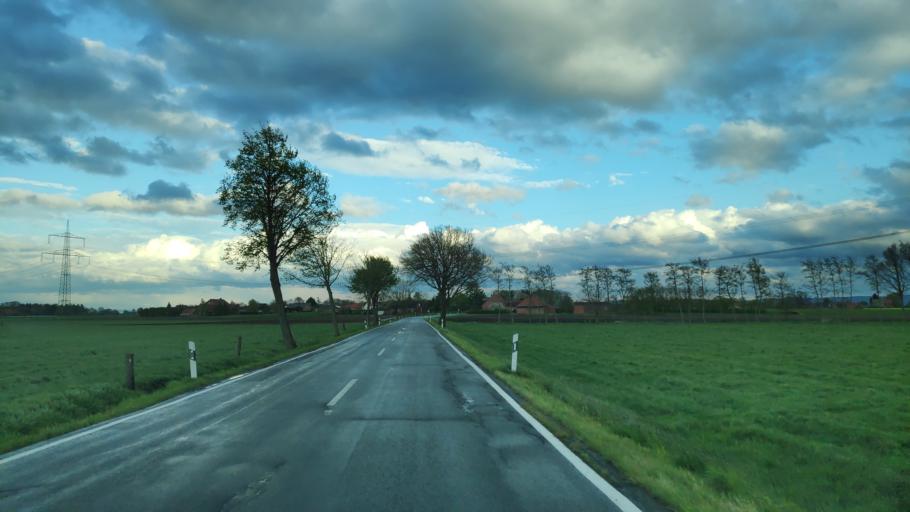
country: DE
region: North Rhine-Westphalia
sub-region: Regierungsbezirk Detmold
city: Hille
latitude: 52.3452
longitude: 8.8258
